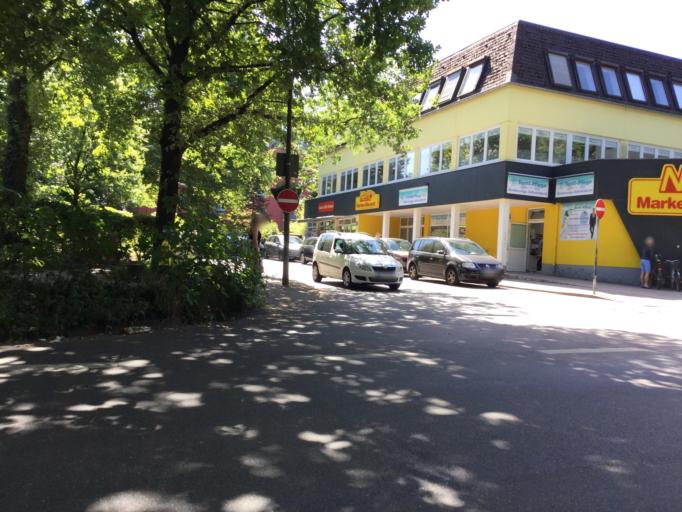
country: DE
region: Hamburg
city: Bergstedt
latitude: 53.6479
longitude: 10.1613
